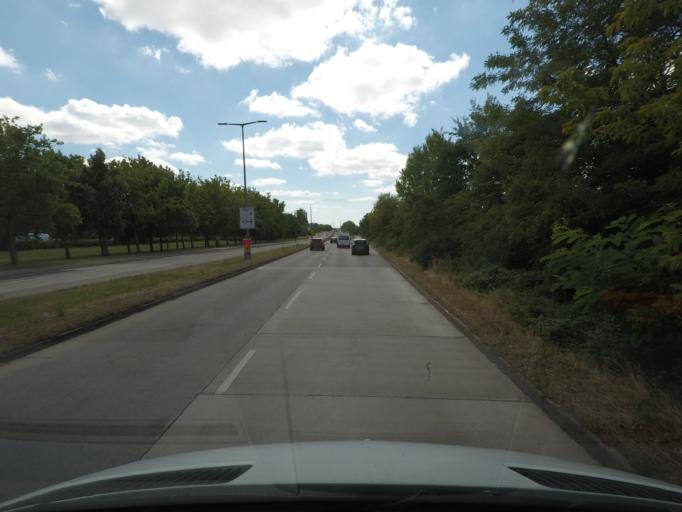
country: DE
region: Berlin
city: Falkenberg
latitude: 52.5663
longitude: 13.5615
